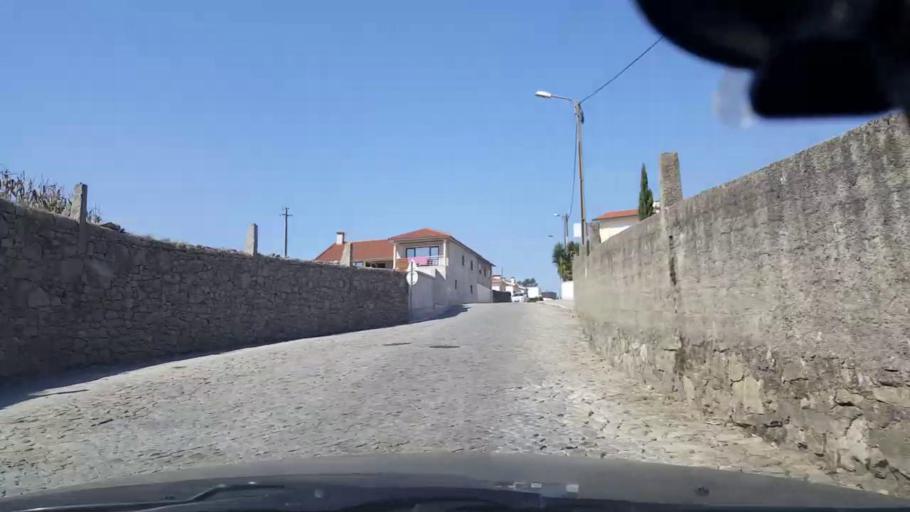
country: PT
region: Porto
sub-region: Vila do Conde
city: Arvore
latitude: 41.3755
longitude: -8.7025
